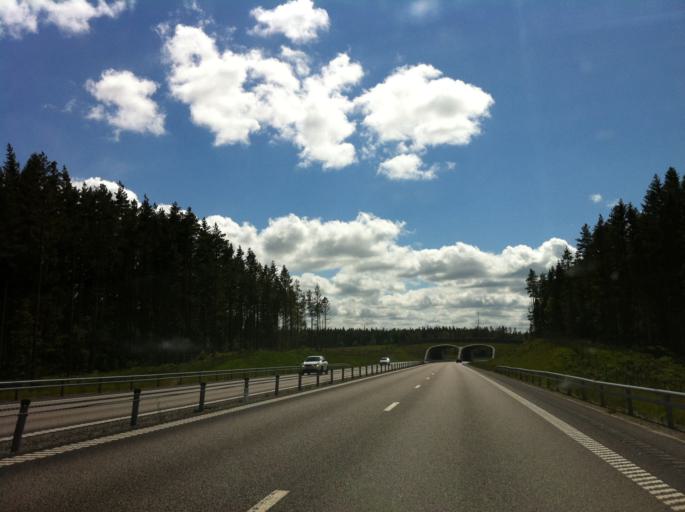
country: SE
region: Vaestra Goetaland
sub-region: Trollhattan
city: Sjuntorp
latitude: 58.2276
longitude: 12.2180
